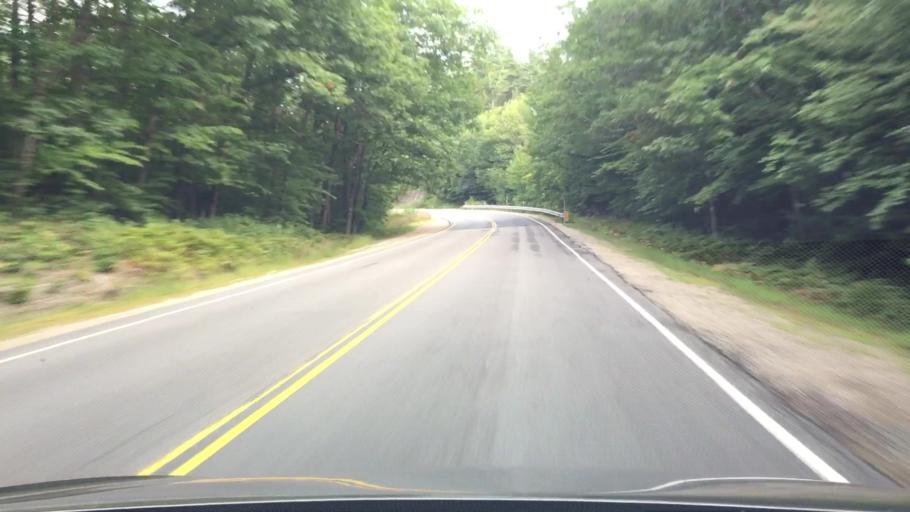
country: US
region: New Hampshire
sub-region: Carroll County
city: Conway
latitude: 44.0012
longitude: -71.2368
